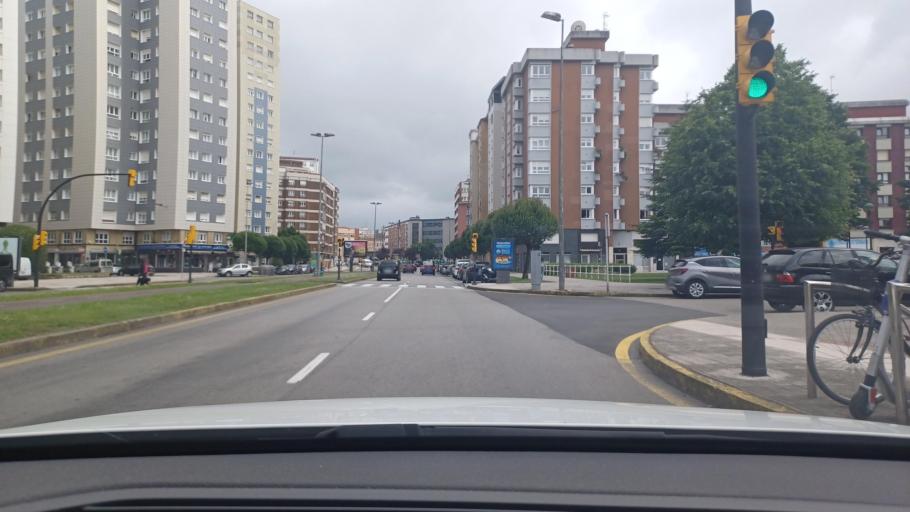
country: ES
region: Asturias
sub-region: Province of Asturias
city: Gijon
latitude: 43.5351
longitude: -5.6719
